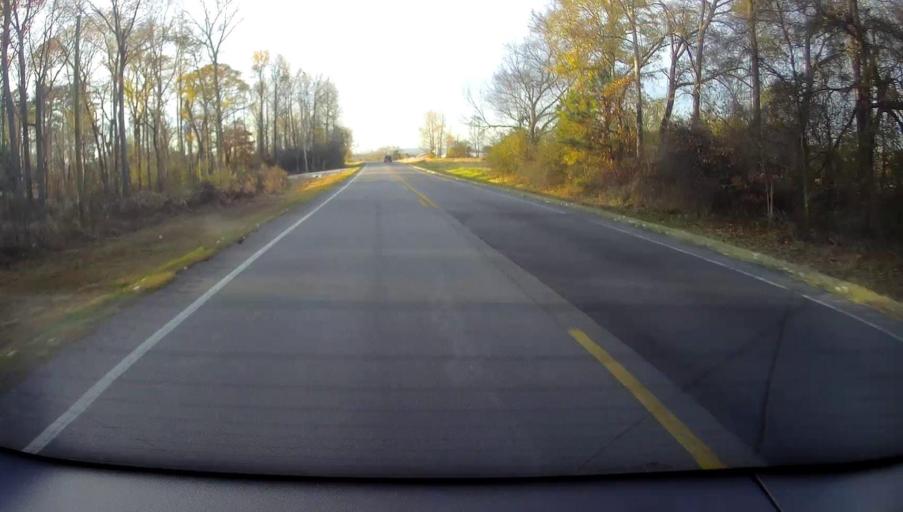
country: US
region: Alabama
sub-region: Blount County
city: Oneonta
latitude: 34.1246
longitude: -86.4028
